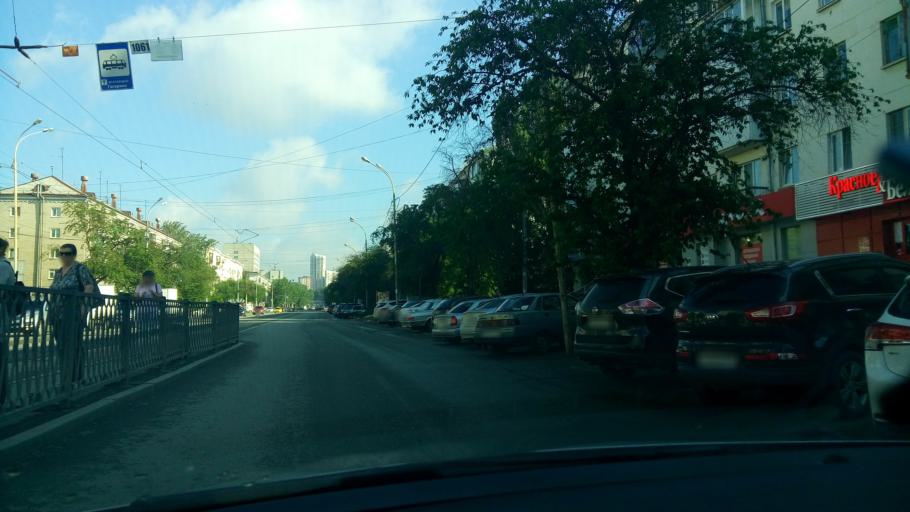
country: RU
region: Sverdlovsk
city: Yekaterinburg
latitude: 56.8401
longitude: 60.6466
